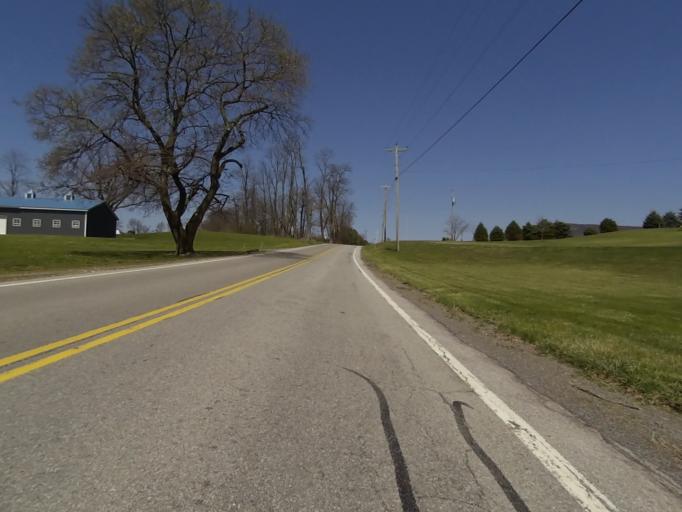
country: US
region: Pennsylvania
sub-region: Blair County
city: Tyrone
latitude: 40.5885
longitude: -78.1392
